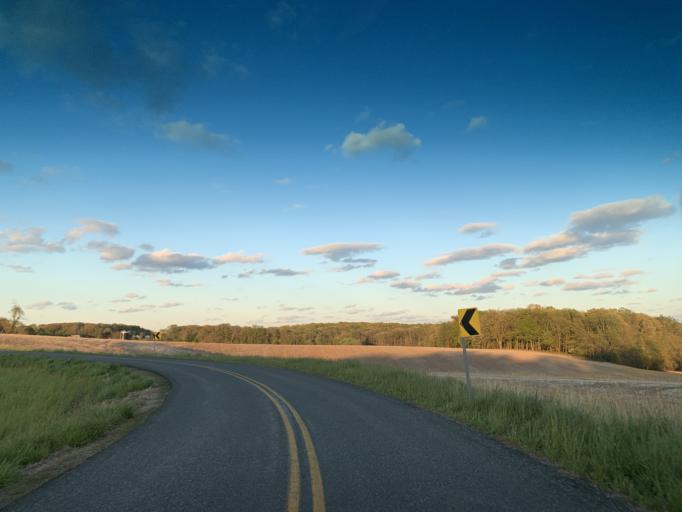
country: US
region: Maryland
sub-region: Harford County
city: Jarrettsville
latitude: 39.6585
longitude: -76.4155
